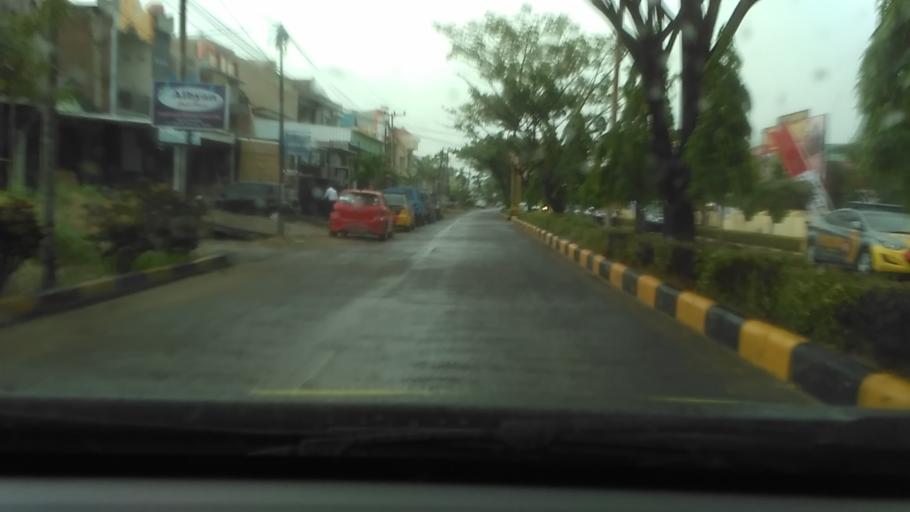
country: ID
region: South Sulawesi
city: Pinrang
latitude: -3.8096
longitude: 119.6478
